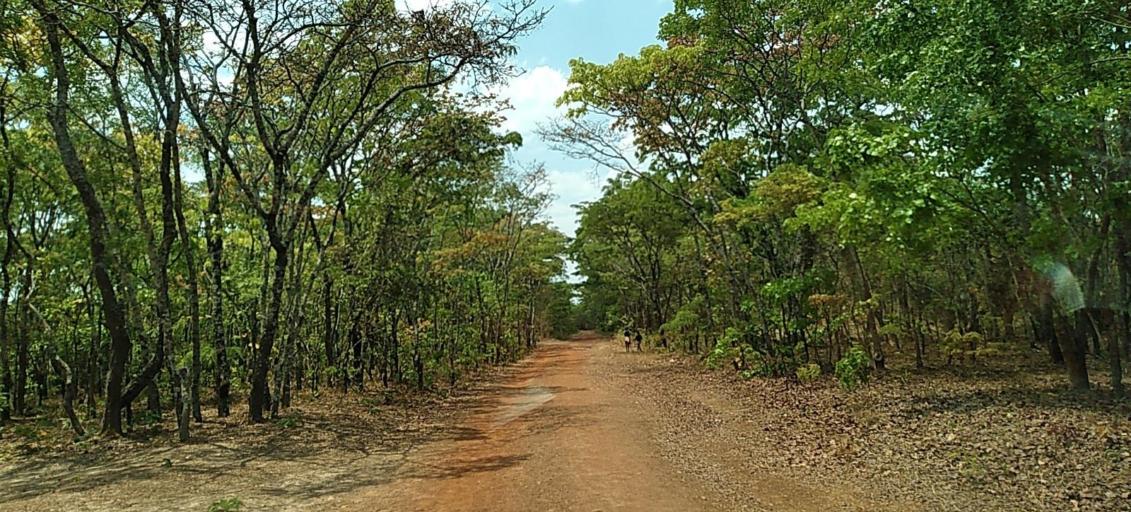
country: ZM
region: Copperbelt
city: Chililabombwe
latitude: -12.4926
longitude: 27.6363
